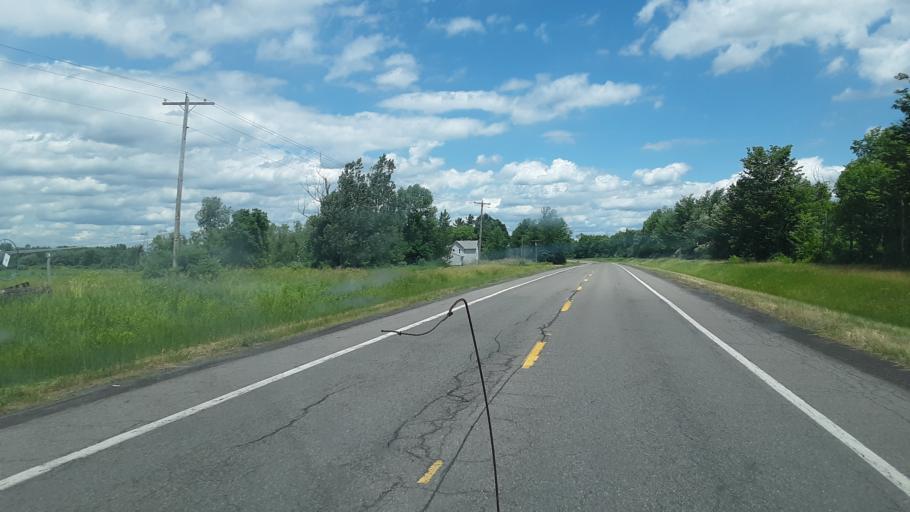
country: US
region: New York
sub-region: Madison County
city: Oneida
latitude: 43.1658
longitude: -75.6561
